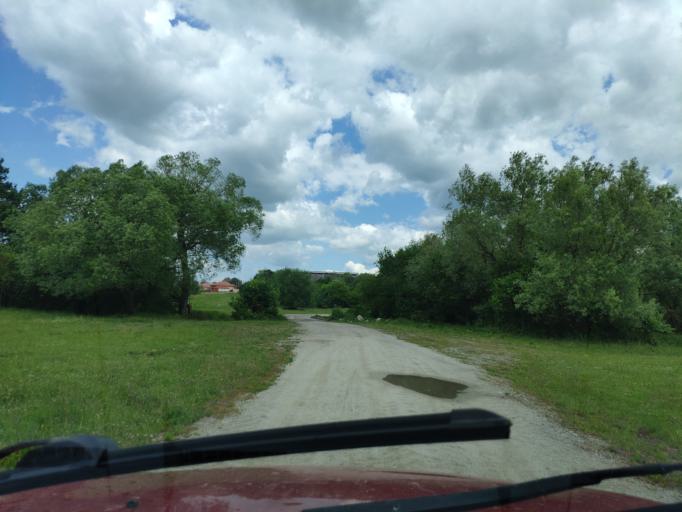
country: SK
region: Kosicky
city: Kosice
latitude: 48.8416
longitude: 21.3211
